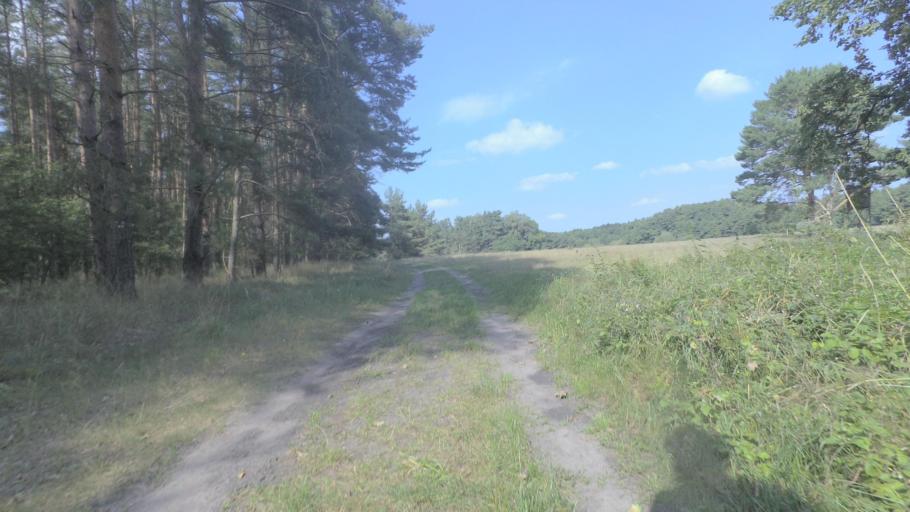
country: DE
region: Brandenburg
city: Rangsdorf
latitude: 52.2489
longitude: 13.4053
